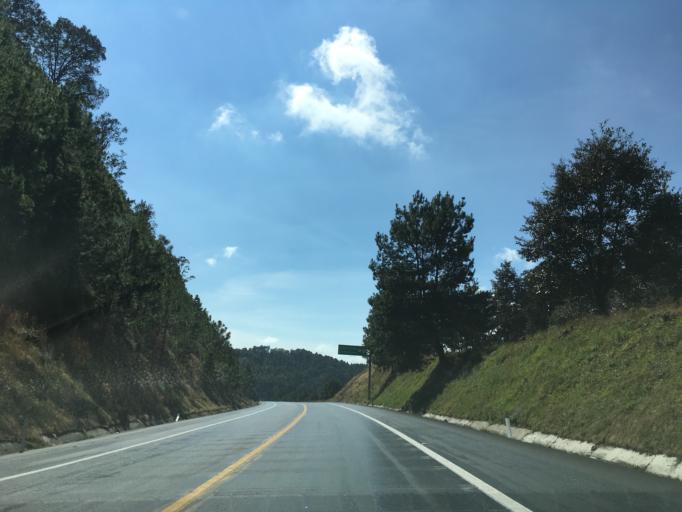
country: MX
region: Michoacan
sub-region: Patzcuaro
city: Santa Maria Huiramangaro (San Juan Tumbio)
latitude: 19.4862
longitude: -101.7229
